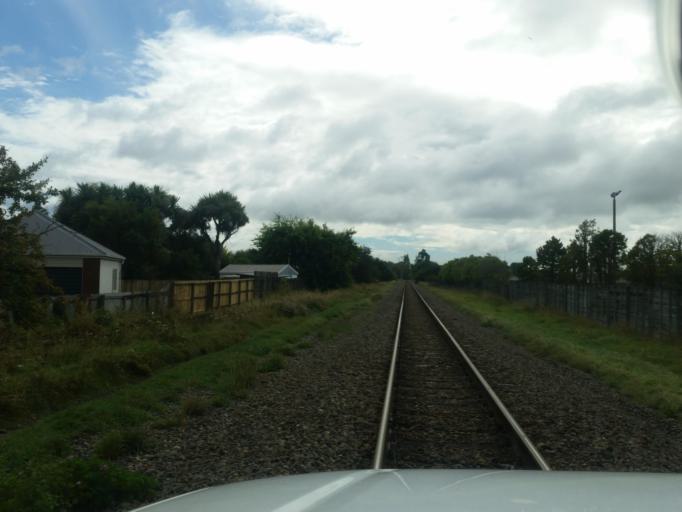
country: NZ
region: Canterbury
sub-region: Christchurch City
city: Christchurch
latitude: -43.4794
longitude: 172.6092
